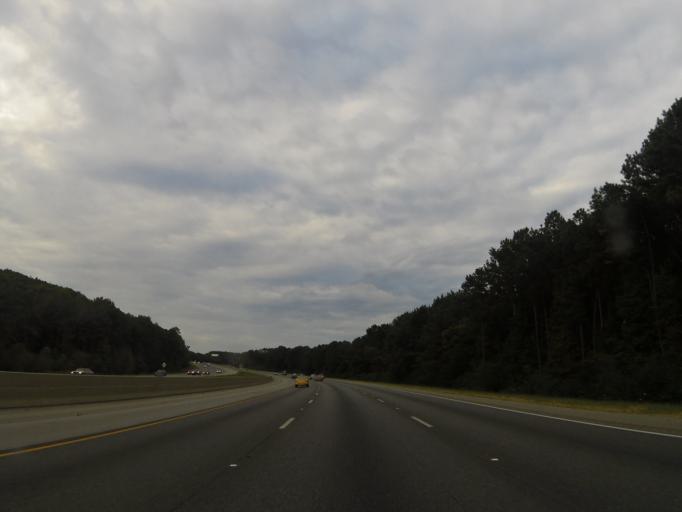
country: US
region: Alabama
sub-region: Shelby County
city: Pelham
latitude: 33.3112
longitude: -86.7867
